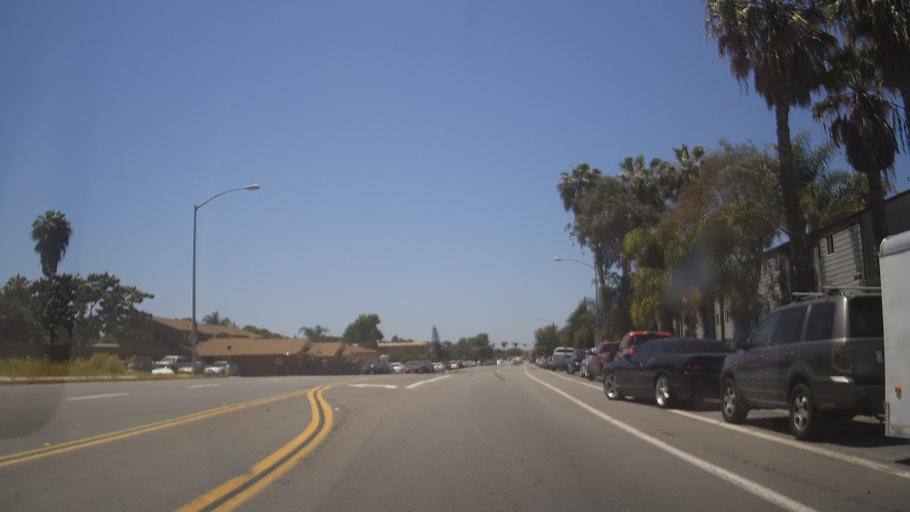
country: US
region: California
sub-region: San Diego County
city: National City
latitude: 32.7078
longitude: -117.0760
